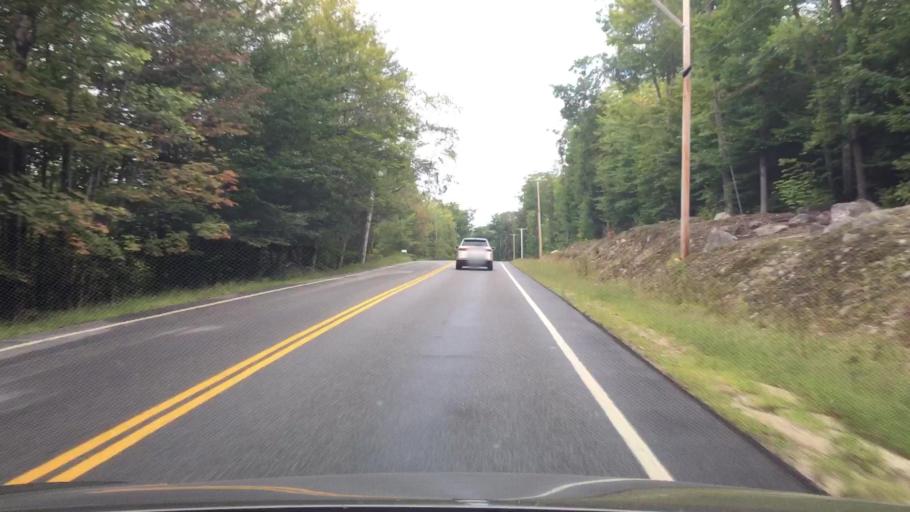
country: US
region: Maine
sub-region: Oxford County
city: Hartford
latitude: 44.3589
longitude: -70.3086
